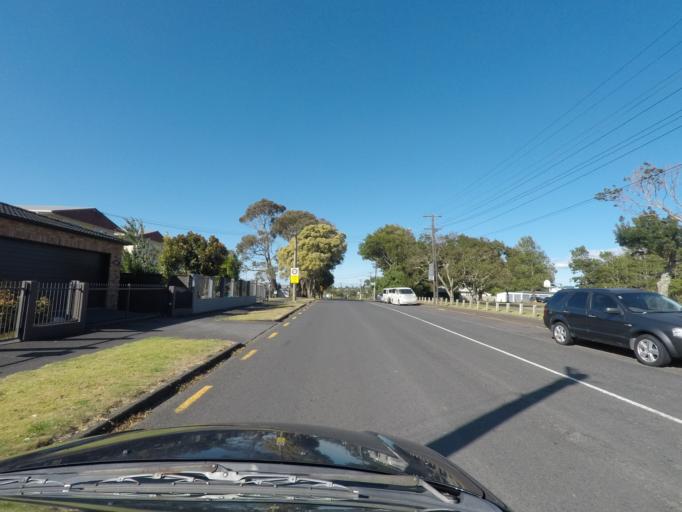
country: NZ
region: Auckland
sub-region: Auckland
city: Rosebank
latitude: -36.8865
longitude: 174.6865
